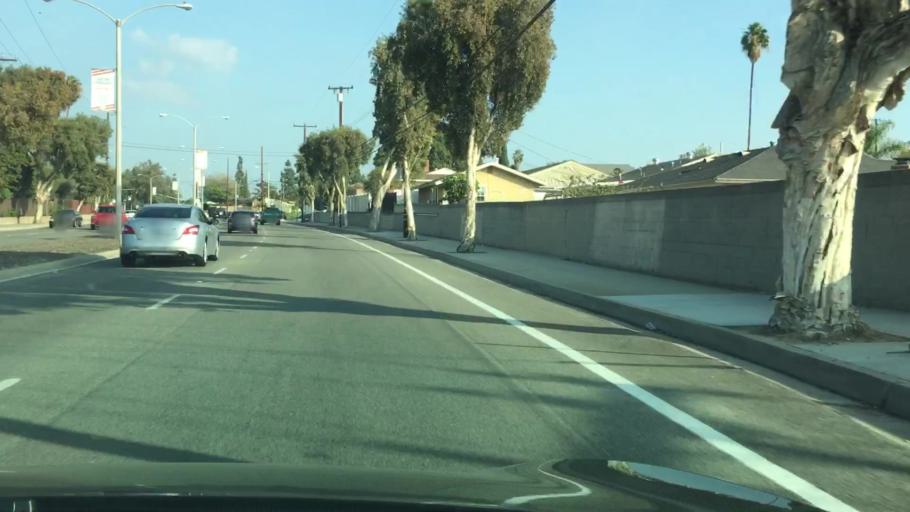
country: US
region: California
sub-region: Los Angeles County
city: La Mirada
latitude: 33.8984
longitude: -118.0140
